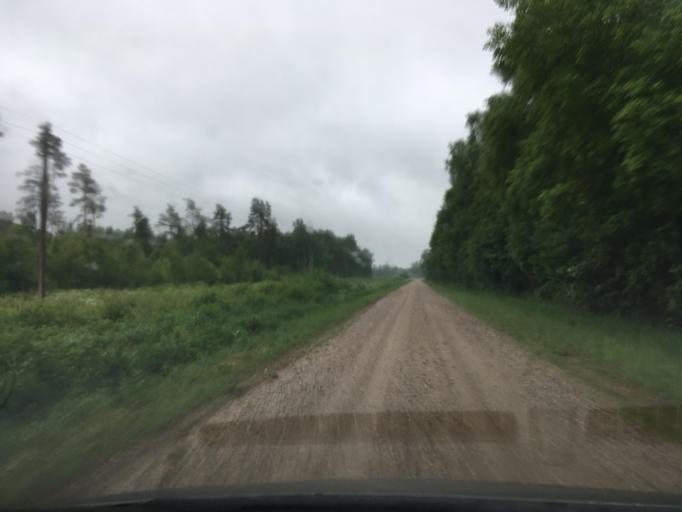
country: EE
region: Laeaene
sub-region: Lihula vald
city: Lihula
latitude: 58.6000
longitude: 23.8373
